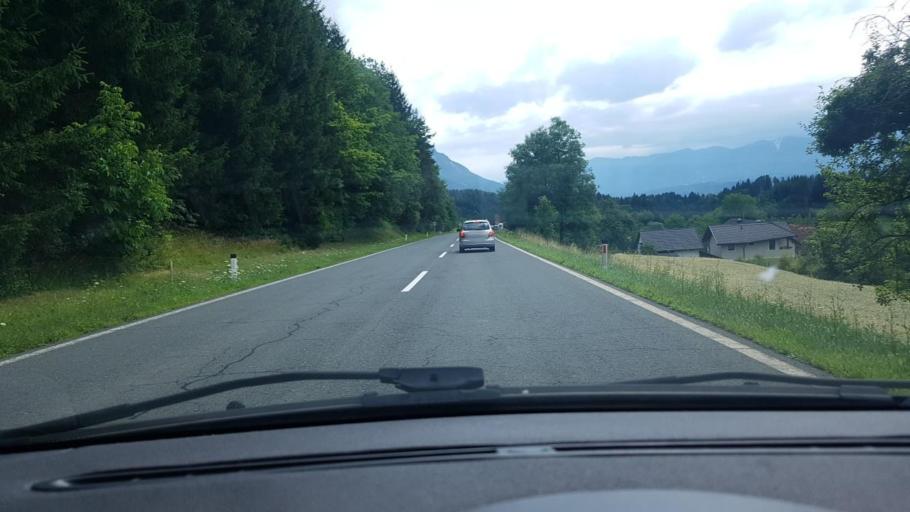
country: AT
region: Carinthia
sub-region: Politischer Bezirk Villach Land
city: Feistritz an der Gail
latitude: 46.6067
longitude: 13.5480
